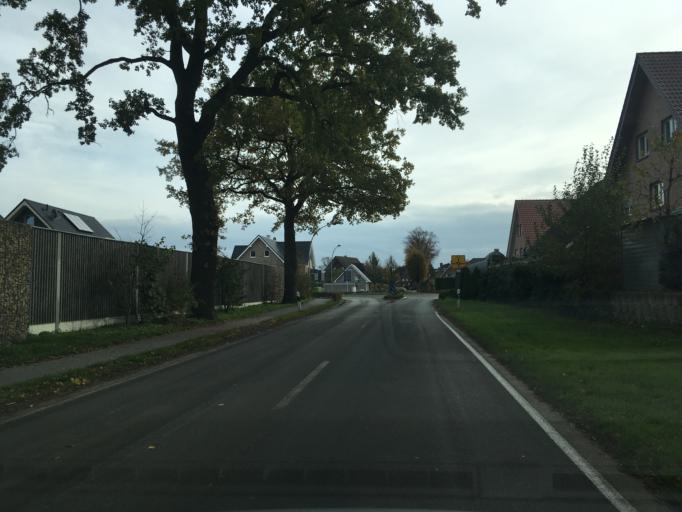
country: DE
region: North Rhine-Westphalia
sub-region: Regierungsbezirk Munster
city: Klein Reken
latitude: 51.8420
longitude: 7.0912
